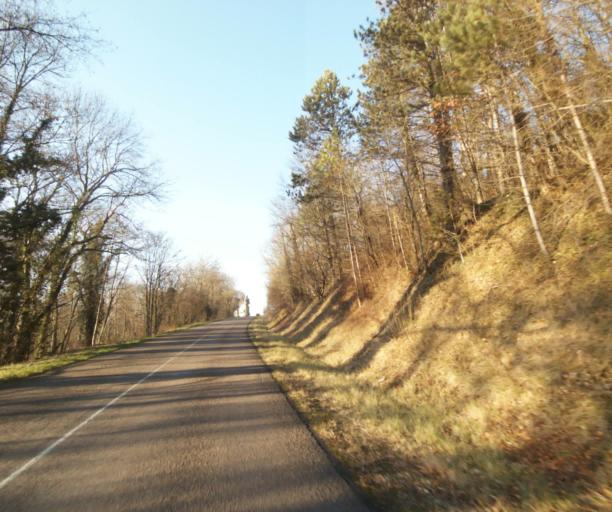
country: FR
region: Champagne-Ardenne
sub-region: Departement de la Haute-Marne
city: Bienville
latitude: 48.5673
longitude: 5.0508
